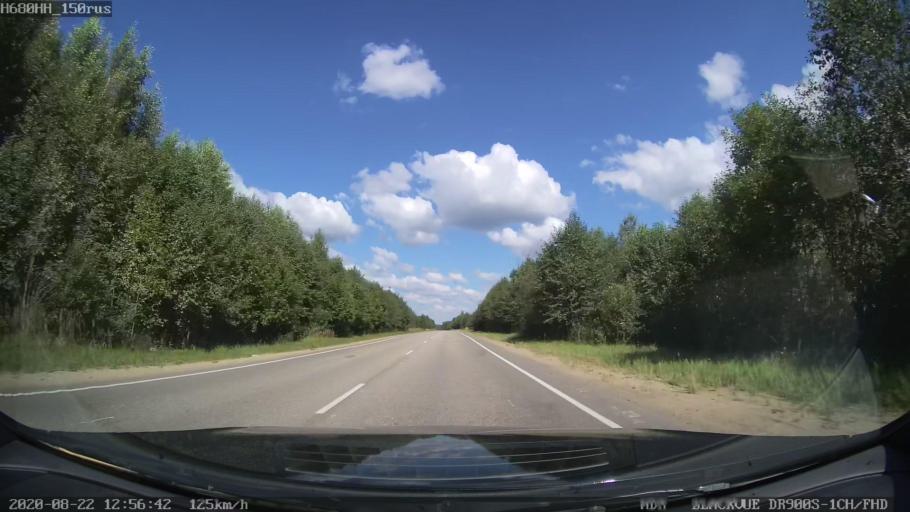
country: RU
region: Tverskaya
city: Rameshki
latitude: 57.5604
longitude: 36.3200
